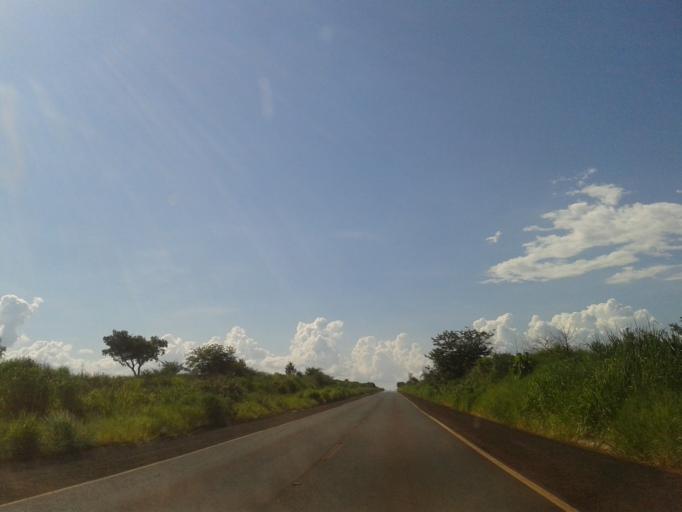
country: BR
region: Minas Gerais
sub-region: Santa Vitoria
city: Santa Vitoria
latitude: -19.0540
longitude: -50.3957
